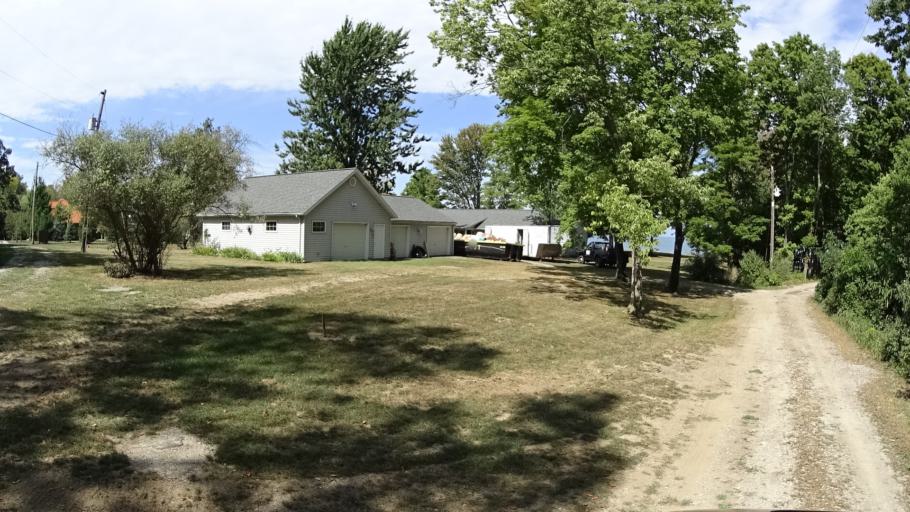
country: US
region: Ohio
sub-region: Erie County
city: Sandusky
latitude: 41.6097
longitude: -82.6922
